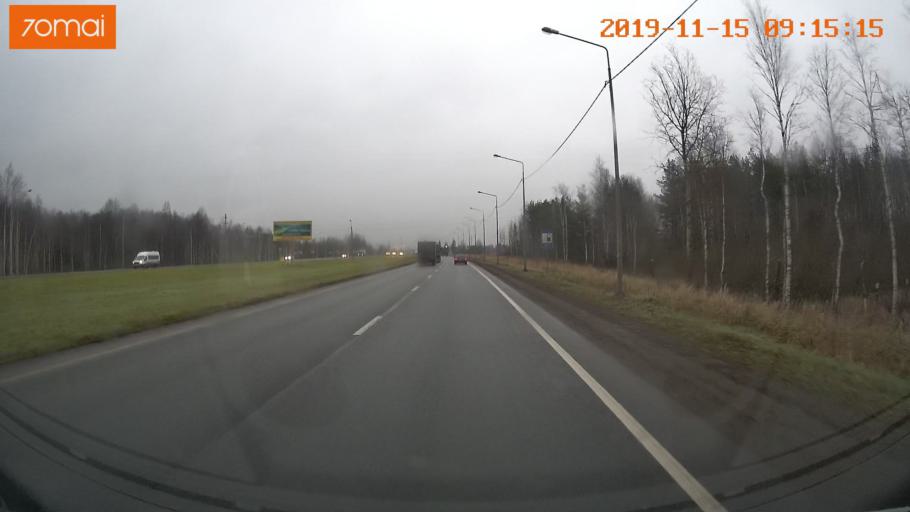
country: RU
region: Vologda
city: Tonshalovo
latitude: 59.2365
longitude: 37.9656
